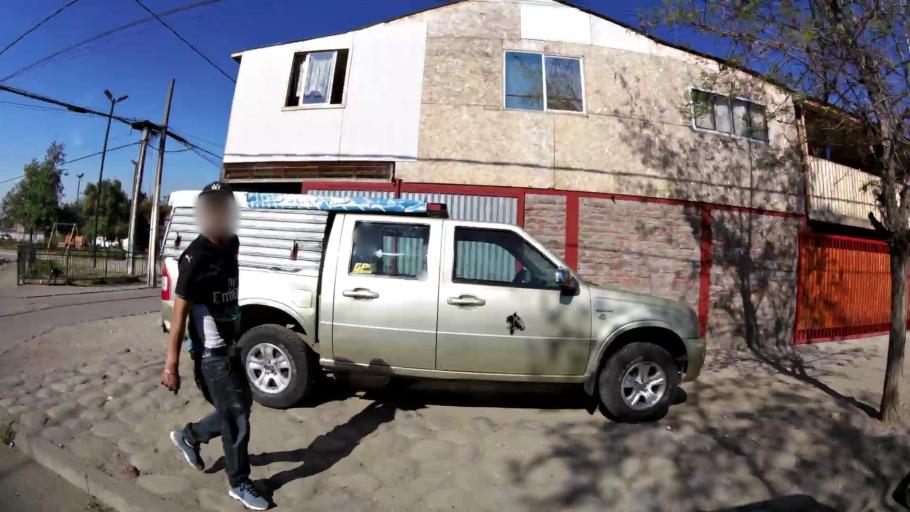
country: CL
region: Santiago Metropolitan
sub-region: Provincia de Santiago
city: La Pintana
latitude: -33.5854
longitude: -70.6507
